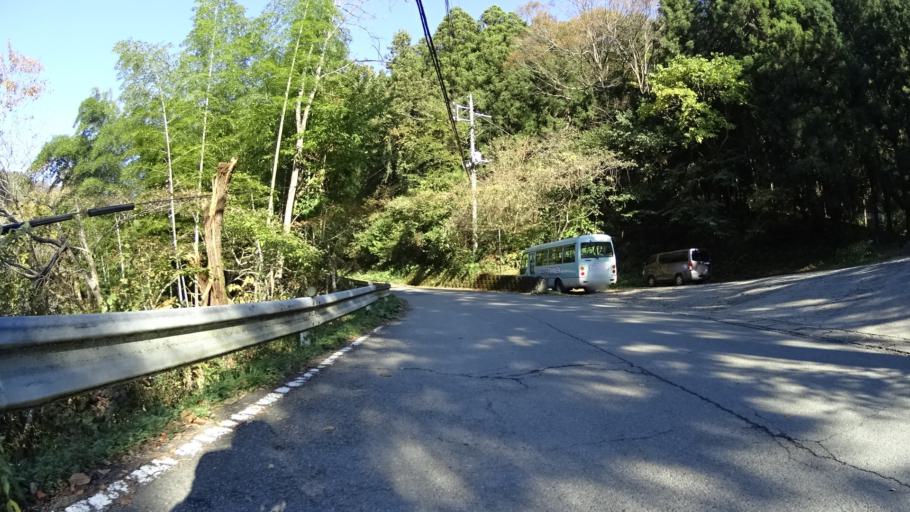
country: JP
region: Yamanashi
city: Uenohara
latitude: 35.6426
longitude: 139.1405
